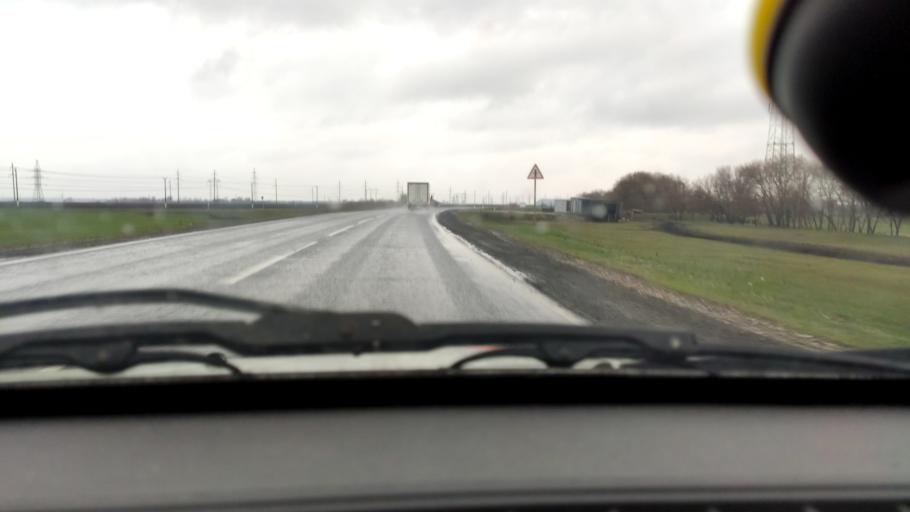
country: RU
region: Samara
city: Povolzhskiy
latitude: 53.6393
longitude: 49.6601
